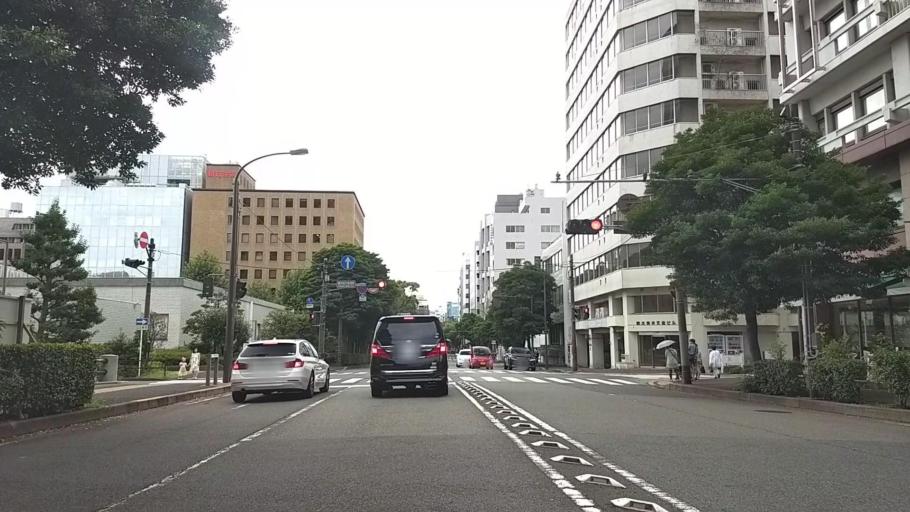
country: JP
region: Kanagawa
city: Yokohama
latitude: 35.4467
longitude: 139.6410
